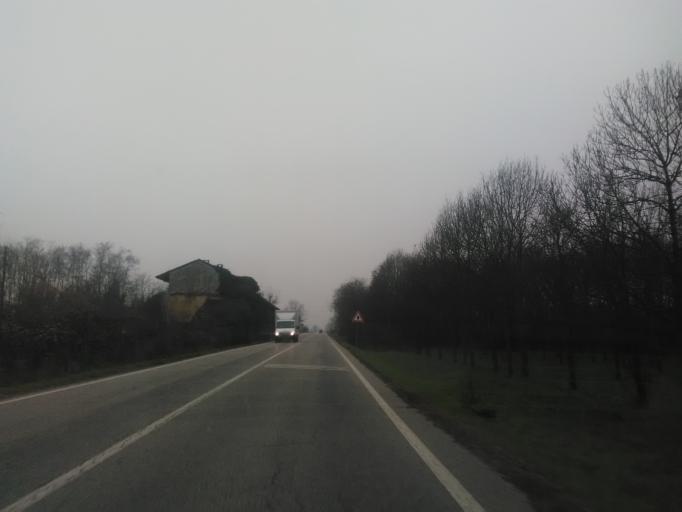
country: IT
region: Piedmont
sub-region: Provincia di Vercelli
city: Bianze
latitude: 45.3285
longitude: 8.1072
